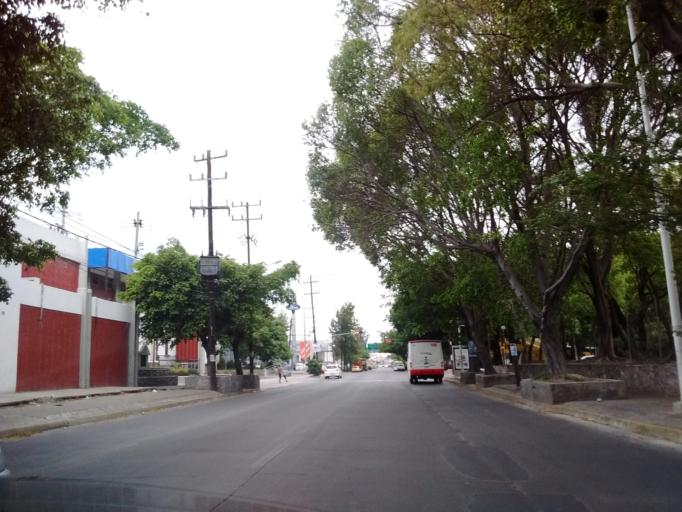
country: MX
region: Jalisco
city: Guadalajara
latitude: 20.6599
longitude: -103.3458
